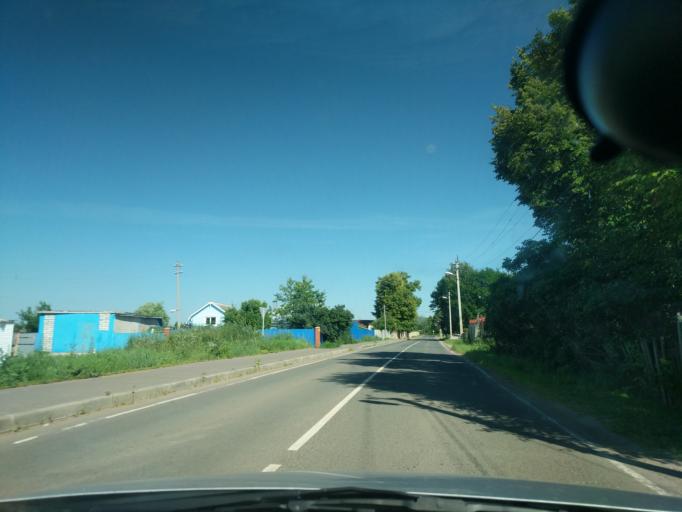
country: RU
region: Moskovskaya
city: Danki
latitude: 54.8446
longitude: 37.5111
